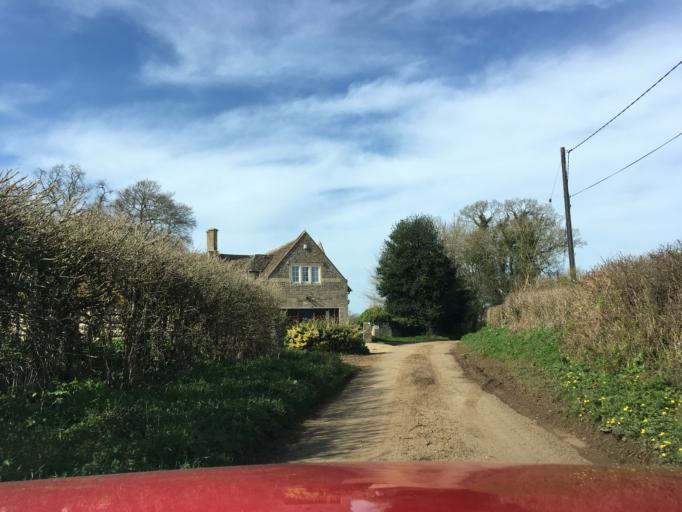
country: GB
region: England
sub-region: Wiltshire
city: Chippenham
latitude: 51.4906
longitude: -2.1426
